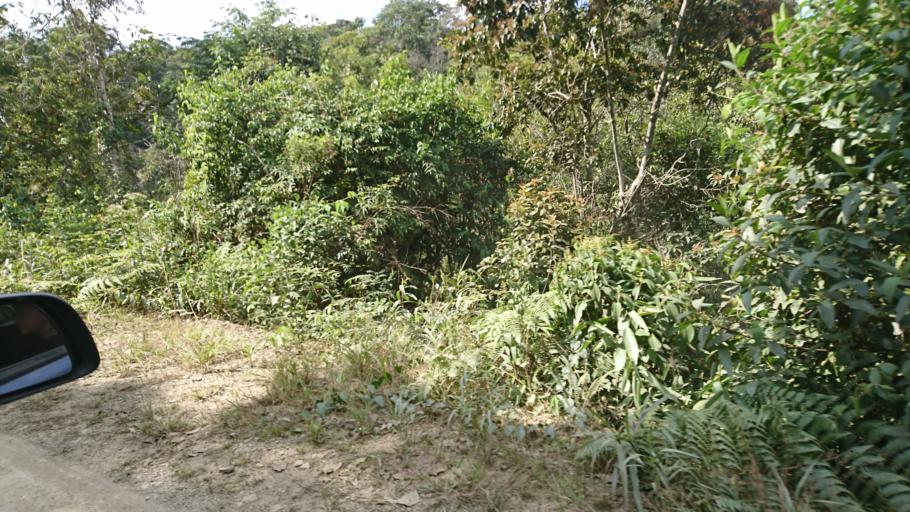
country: BO
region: La Paz
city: Coroico
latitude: -16.0776
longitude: -67.7917
